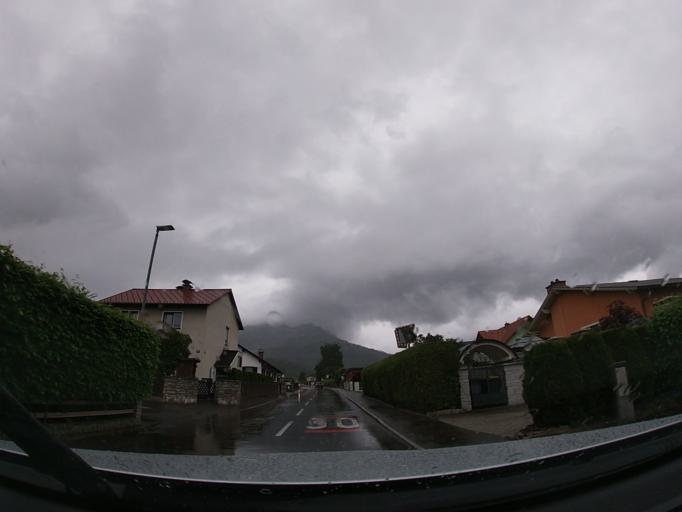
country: AT
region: Styria
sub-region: Politischer Bezirk Leoben
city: Trofaiach
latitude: 47.4257
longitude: 14.9864
